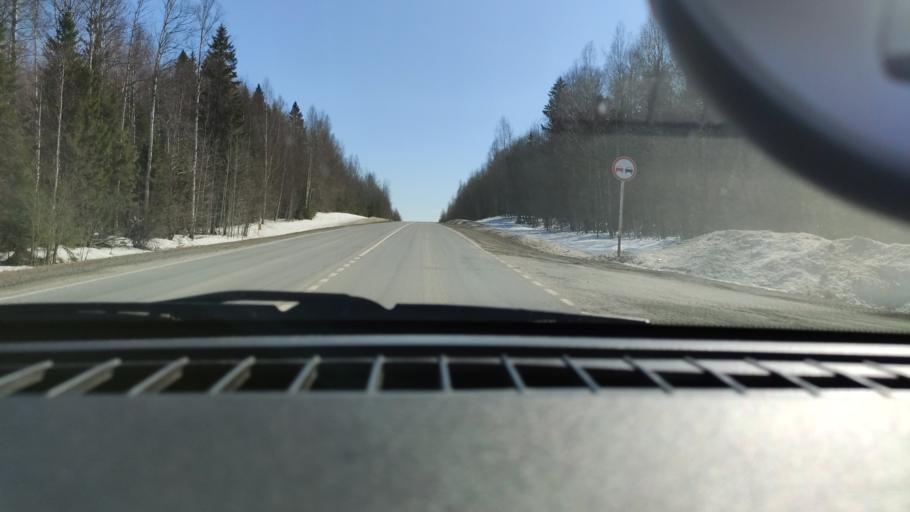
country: RU
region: Perm
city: Perm
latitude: 58.1549
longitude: 56.2521
